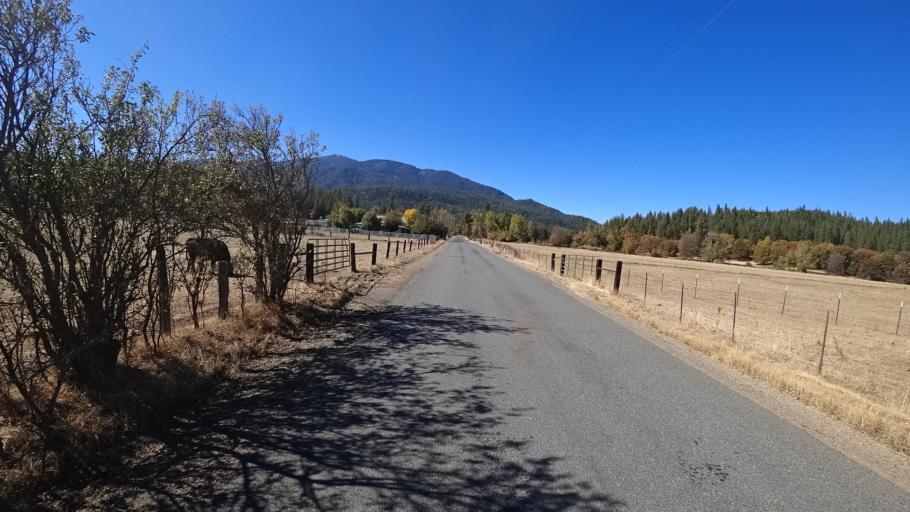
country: US
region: California
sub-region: Siskiyou County
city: Yreka
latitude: 41.6241
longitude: -122.9740
